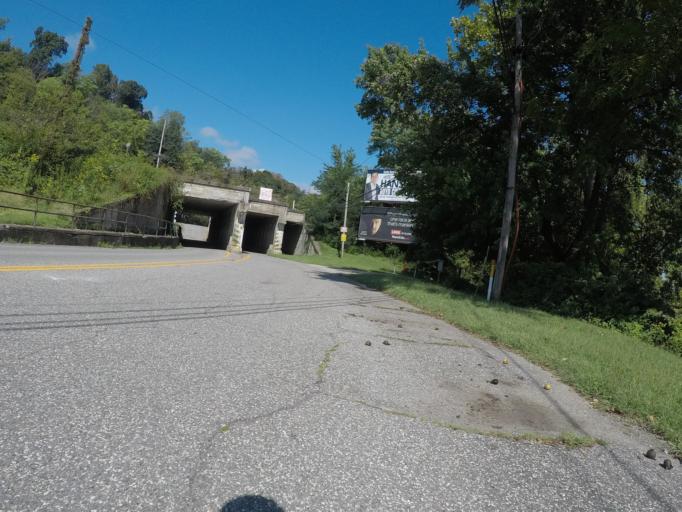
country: US
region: Ohio
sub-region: Lawrence County
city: South Point
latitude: 38.4279
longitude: -82.6021
